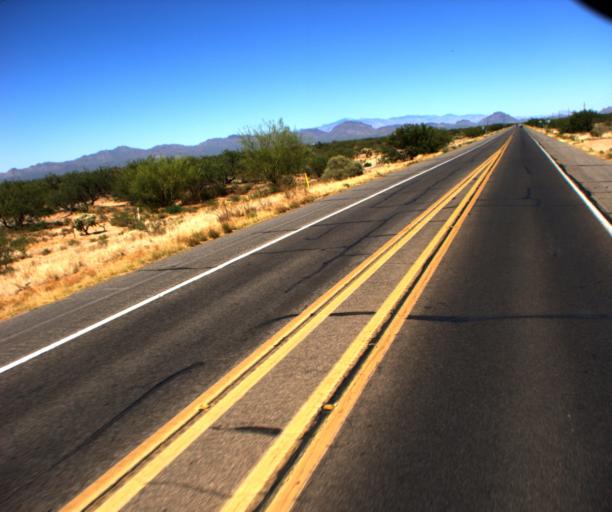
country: US
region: Arizona
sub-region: Pima County
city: Three Points
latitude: 32.0976
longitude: -111.2611
